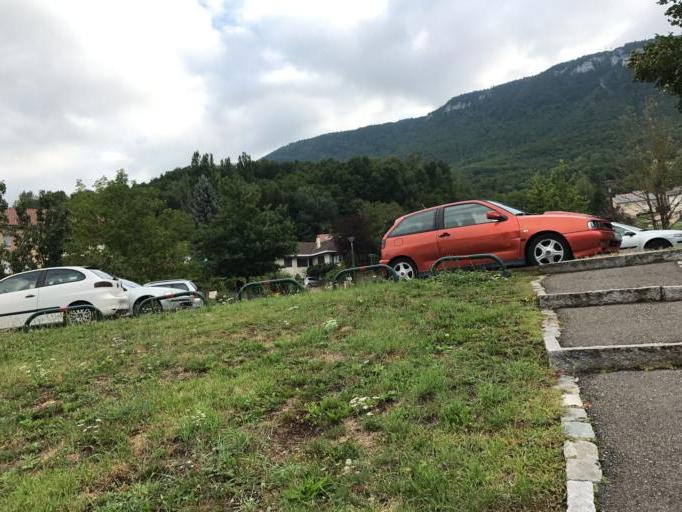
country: FR
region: Rhone-Alpes
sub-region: Departement de l'Ain
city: Lancrans
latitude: 46.1244
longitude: 5.8350
